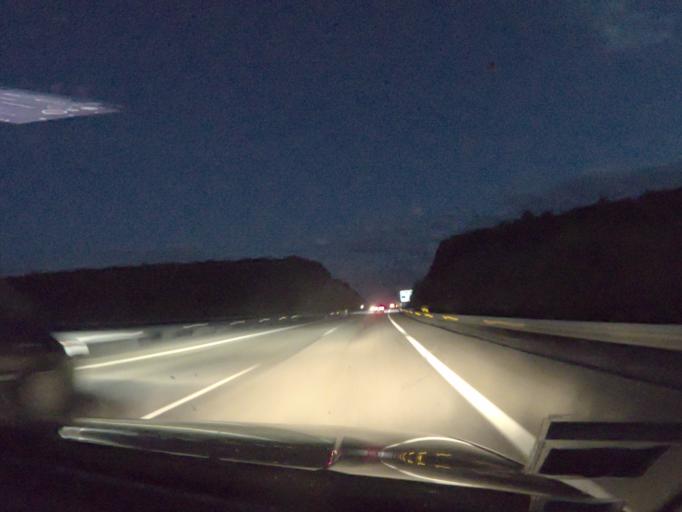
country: ES
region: Castille and Leon
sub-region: Provincia de Leon
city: Brazuelo
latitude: 42.5432
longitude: -6.1594
